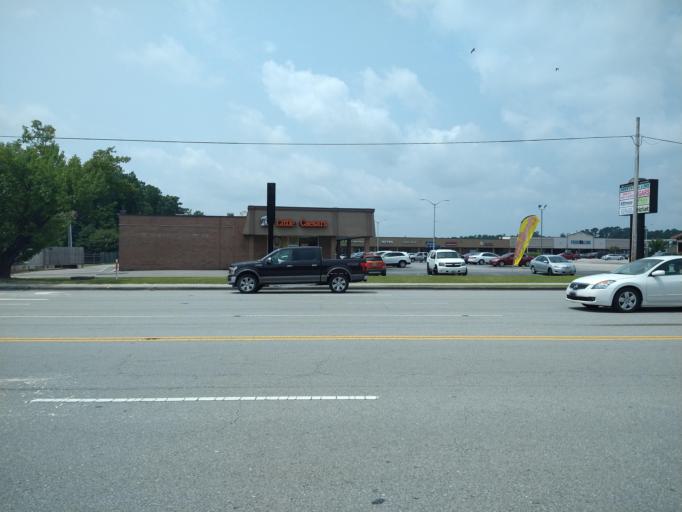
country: US
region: North Carolina
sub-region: Onslow County
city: Pumpkin Center
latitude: 34.7739
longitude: -77.3886
